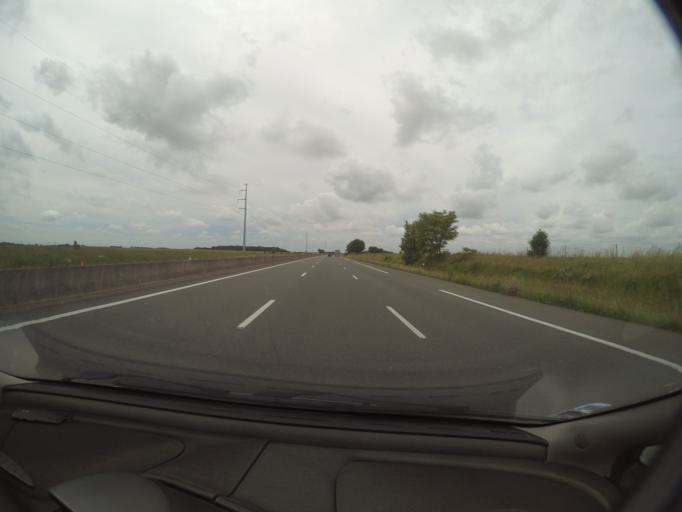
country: FR
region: Centre
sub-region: Departement d'Eure-et-Loir
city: Bailleau-le-Pin
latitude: 48.3408
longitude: 1.4058
